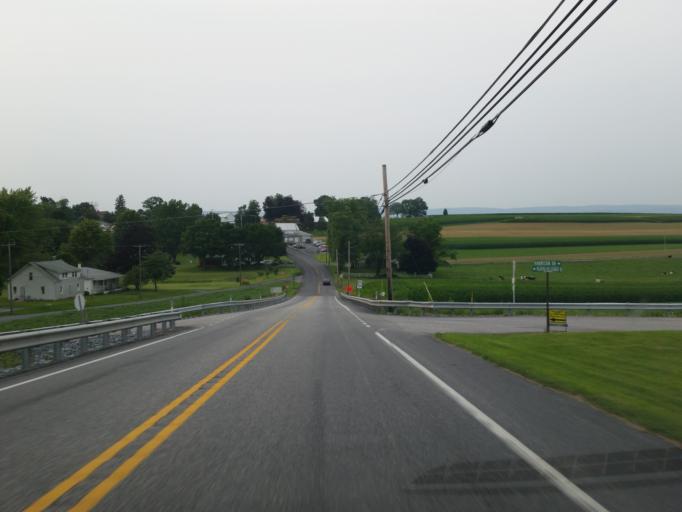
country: US
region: Pennsylvania
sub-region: Lebanon County
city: Annville
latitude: 40.3607
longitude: -76.5471
